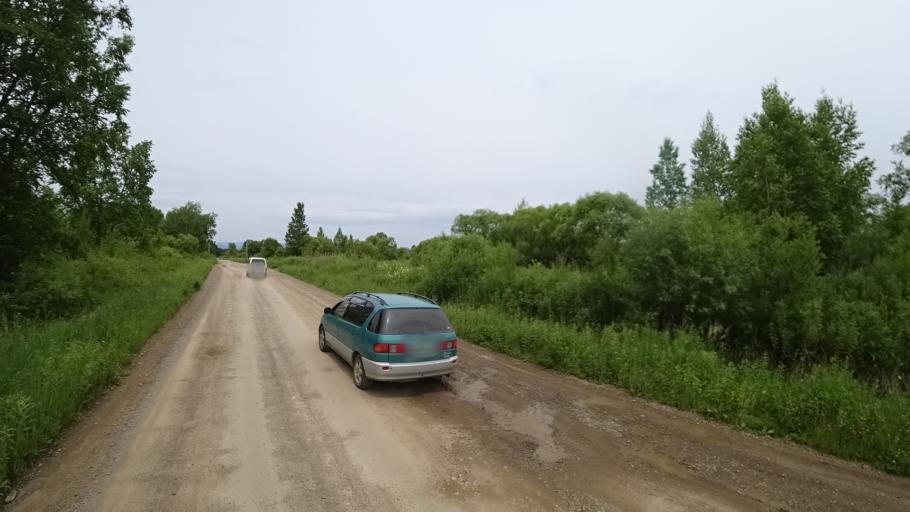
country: RU
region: Primorskiy
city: Arsen'yev
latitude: 44.1940
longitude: 133.3096
